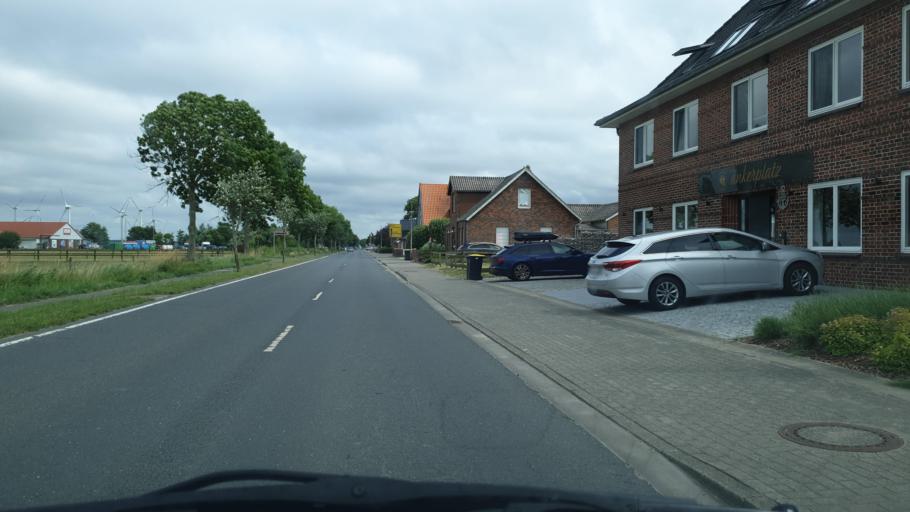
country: DE
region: Schleswig-Holstein
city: Friedrichskoog
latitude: 54.0154
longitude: 8.8938
